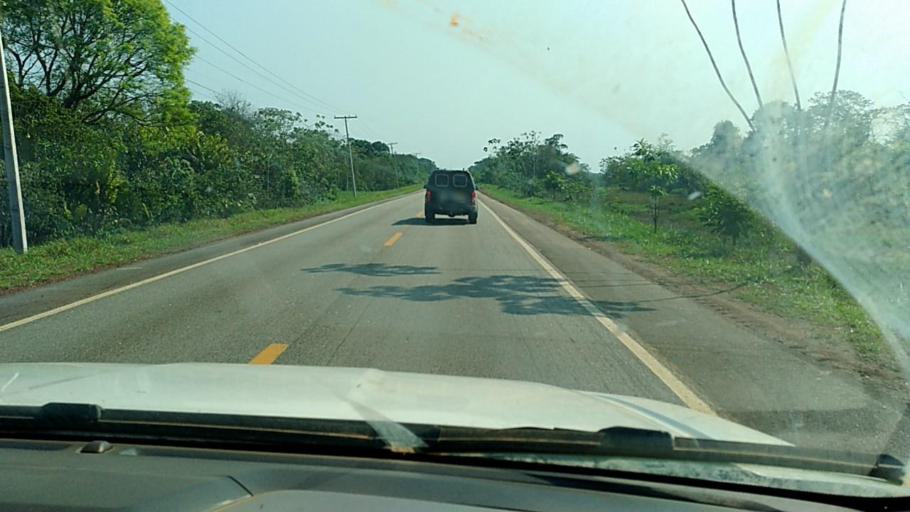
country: BR
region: Amazonas
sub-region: Humaita
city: Humaita
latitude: -7.7644
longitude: -63.1473
